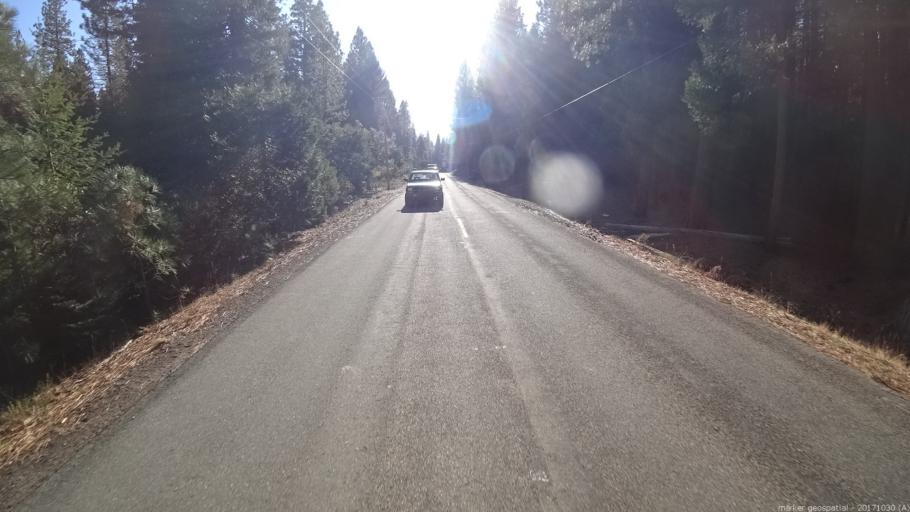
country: US
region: California
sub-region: Shasta County
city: Shingletown
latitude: 40.5310
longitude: -121.7444
